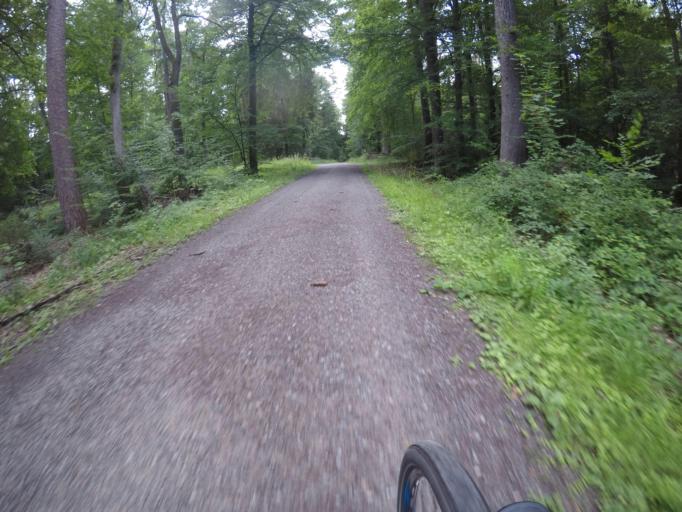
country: DE
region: Baden-Wuerttemberg
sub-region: Regierungsbezirk Stuttgart
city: Gerlingen
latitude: 48.7682
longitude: 9.1069
